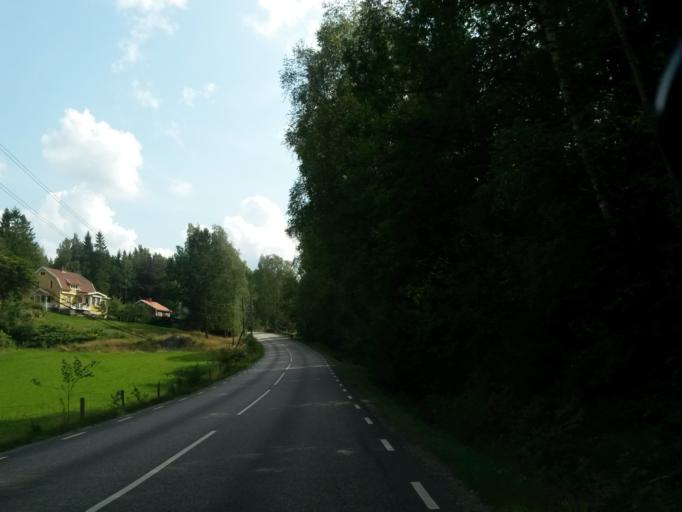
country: SE
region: Vaestra Goetaland
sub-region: Lerums Kommun
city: Lerum
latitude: 57.7681
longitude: 12.3012
